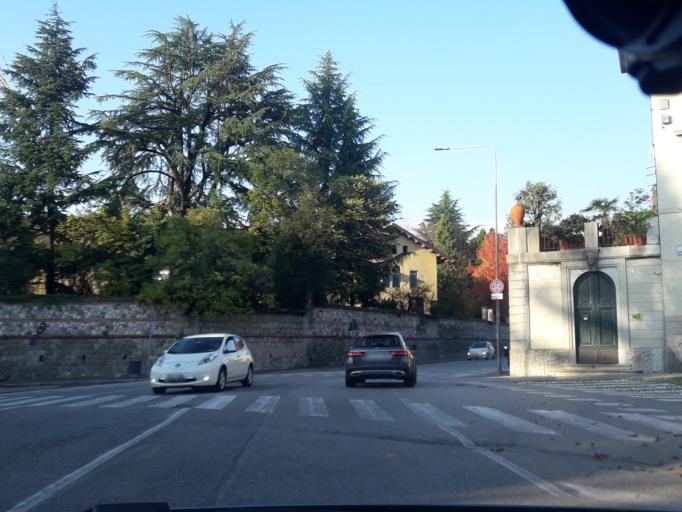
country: IT
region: Friuli Venezia Giulia
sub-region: Provincia di Udine
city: Udine
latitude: 46.0676
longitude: 13.2357
